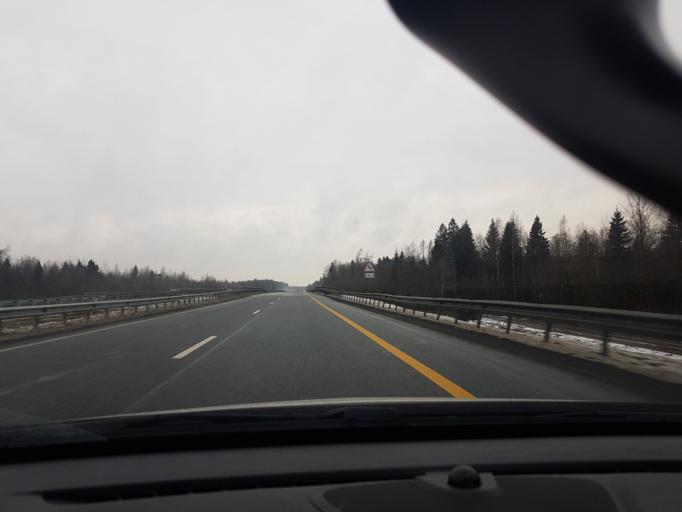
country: RU
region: Moskovskaya
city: Novopetrovskoye
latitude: 55.9817
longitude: 36.4164
